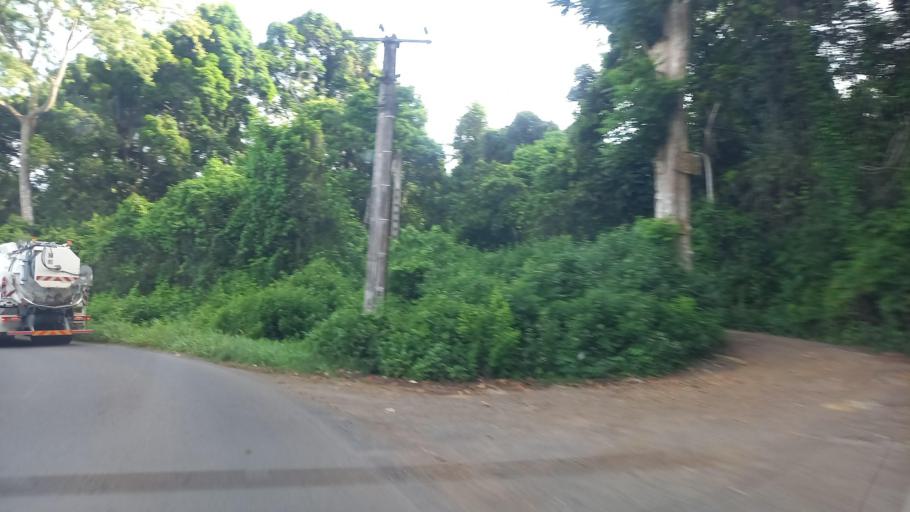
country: YT
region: Chiconi
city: Chiconi
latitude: -12.8093
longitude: 45.1281
